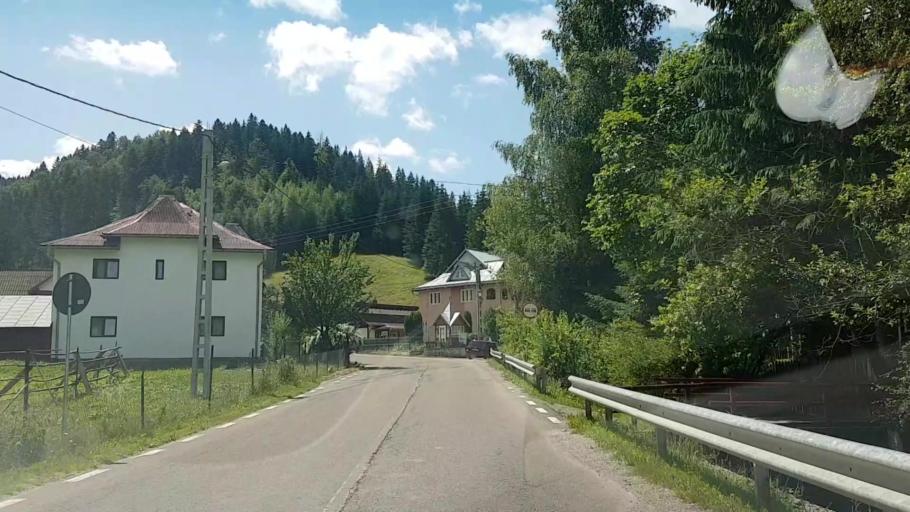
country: RO
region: Suceava
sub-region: Comuna Sadova
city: Sadova
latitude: 47.4828
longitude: 25.4918
